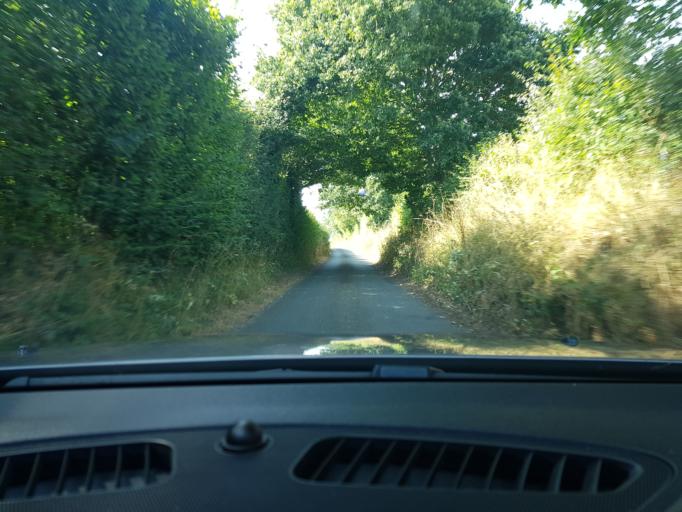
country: GB
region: England
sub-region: West Berkshire
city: Hungerford
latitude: 51.4402
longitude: -1.5063
